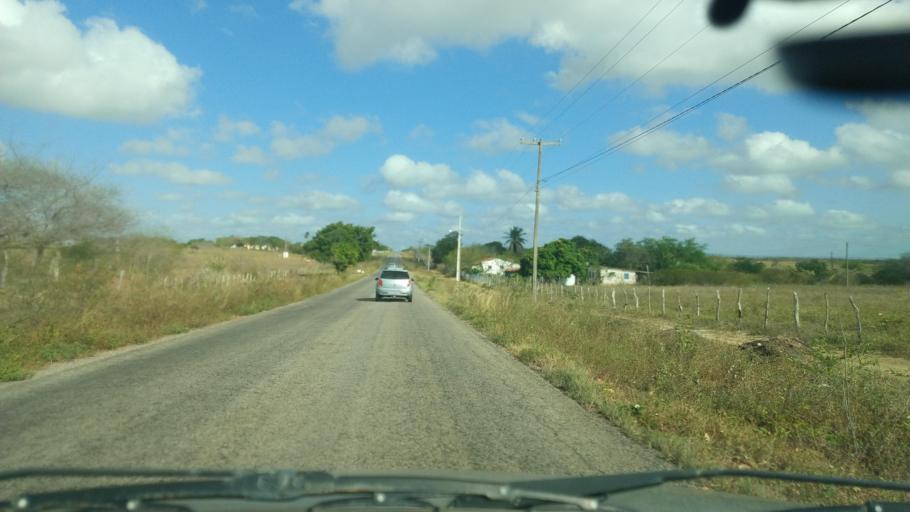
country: BR
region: Rio Grande do Norte
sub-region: Sao Paulo Do Potengi
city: Sao Paulo do Potengi
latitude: -5.9155
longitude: -35.7316
